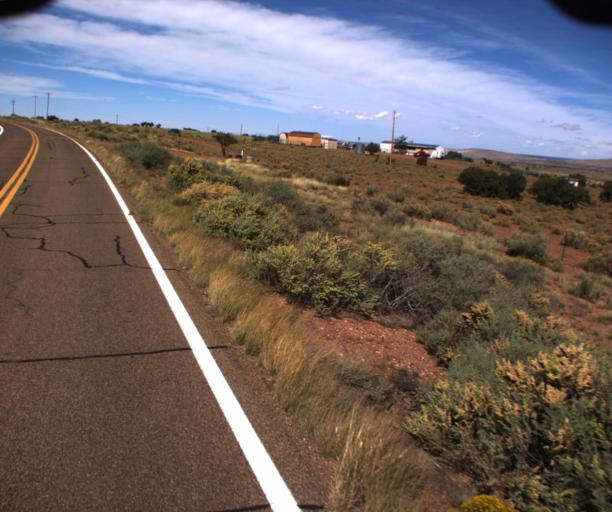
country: US
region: Arizona
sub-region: Apache County
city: Saint Johns
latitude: 34.5541
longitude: -109.6253
